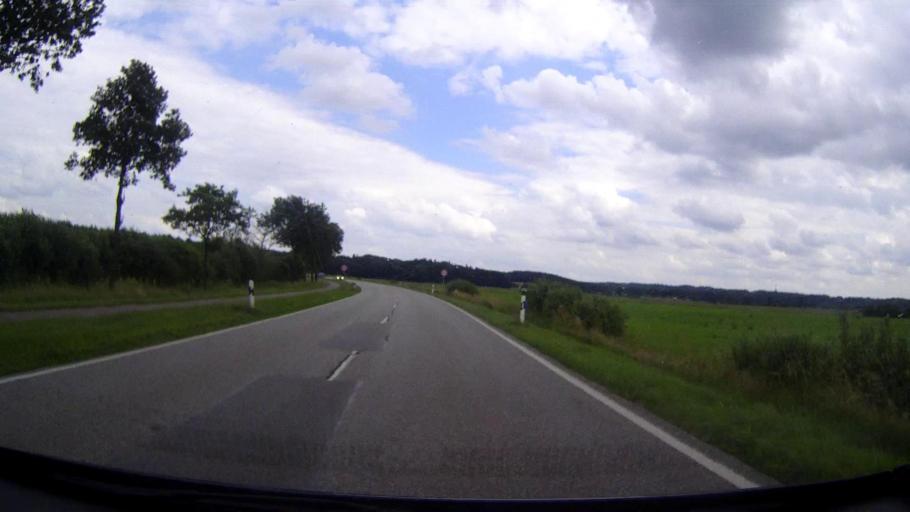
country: DE
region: Schleswig-Holstein
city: Tappendorf
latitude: 54.0807
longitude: 9.6978
